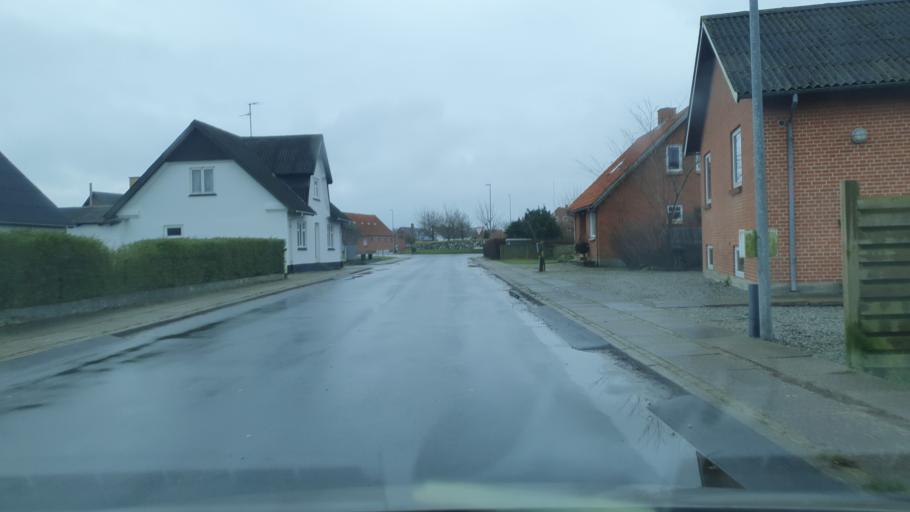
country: DK
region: North Denmark
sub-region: Jammerbugt Kommune
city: Fjerritslev
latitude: 57.1041
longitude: 9.1242
